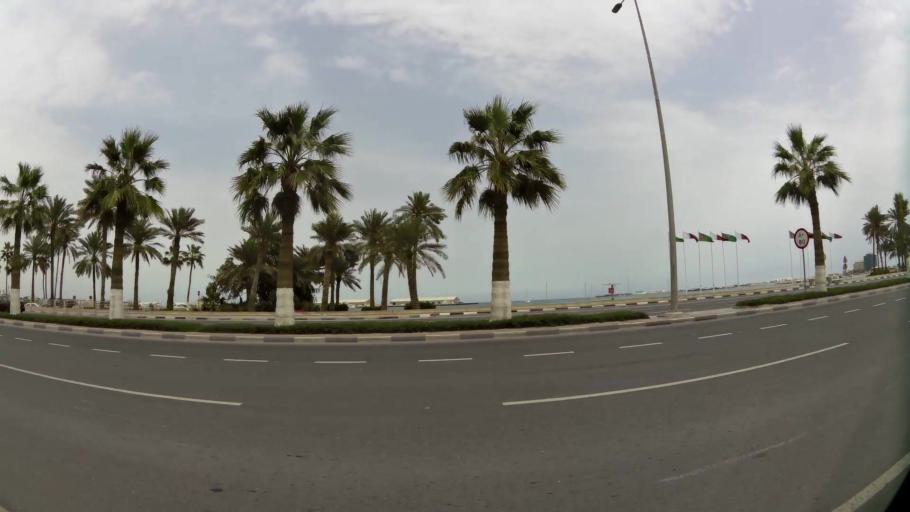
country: QA
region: Baladiyat ad Dawhah
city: Doha
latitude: 25.2898
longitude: 51.5493
